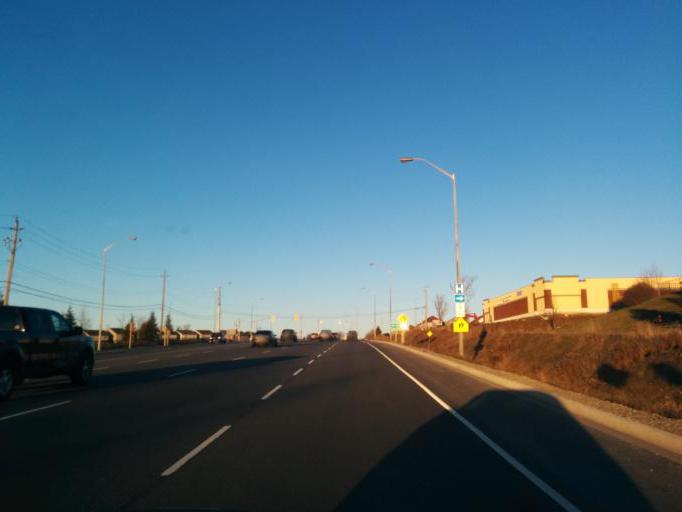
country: CA
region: Ontario
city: Orangeville
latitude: 43.9209
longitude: -80.0752
